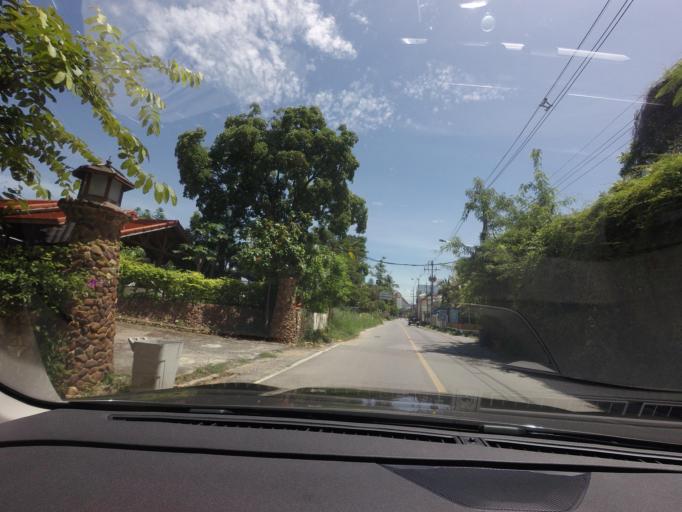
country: TH
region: Prachuap Khiri Khan
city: Hua Hin
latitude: 12.5120
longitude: 99.9758
